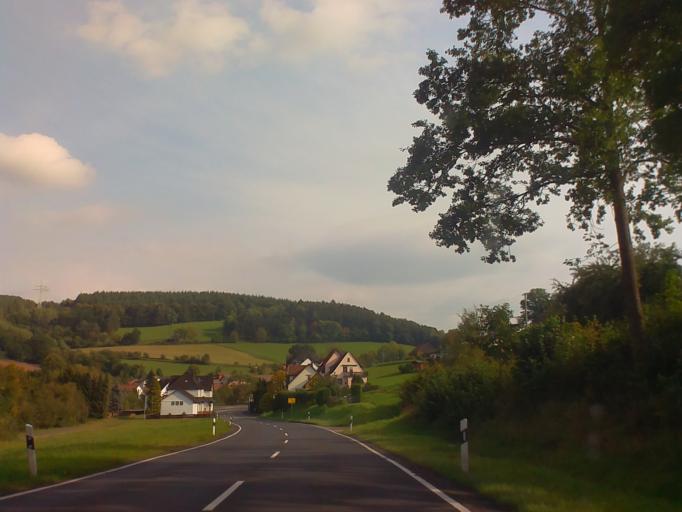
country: DE
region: Hesse
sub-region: Regierungsbezirk Kassel
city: Schenklengsfeld
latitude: 50.8550
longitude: 9.8147
